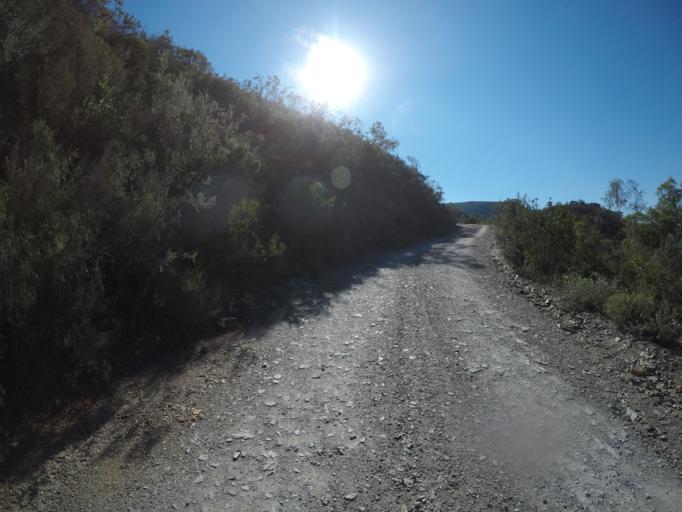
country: ZA
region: Eastern Cape
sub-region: Cacadu District Municipality
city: Kareedouw
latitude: -33.6543
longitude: 24.5081
